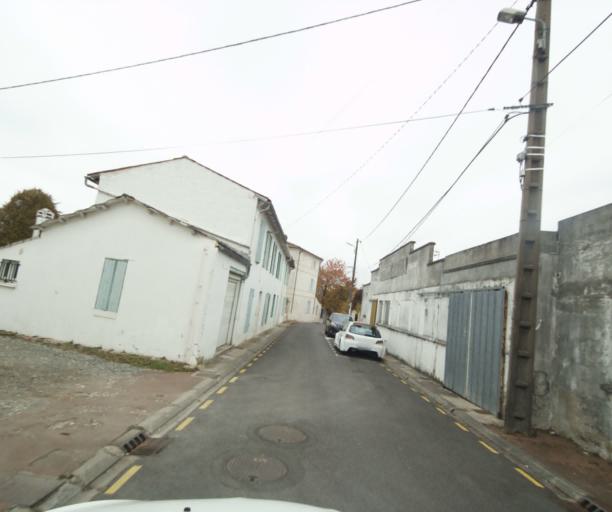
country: FR
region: Poitou-Charentes
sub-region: Departement de la Charente-Maritime
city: Saintes
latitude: 45.7396
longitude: -0.6229
